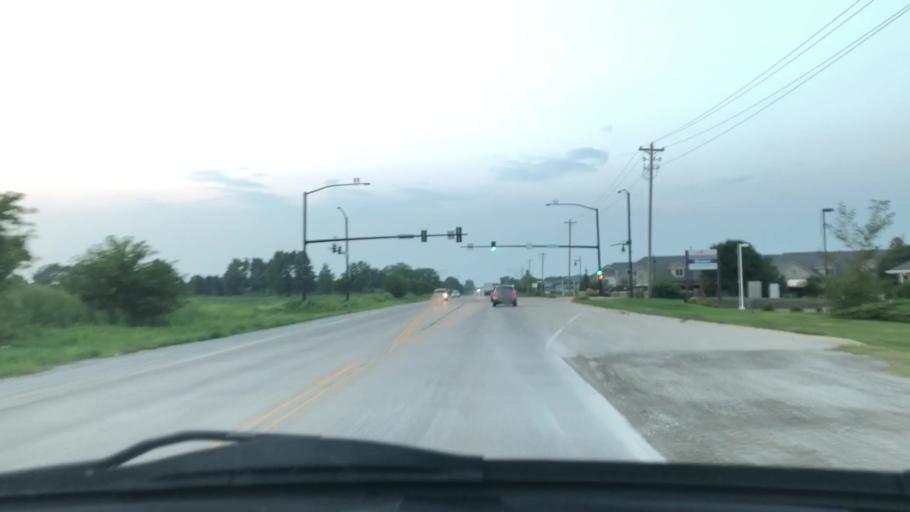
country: US
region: Iowa
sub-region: Johnson County
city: North Liberty
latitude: 41.7280
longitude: -91.6077
